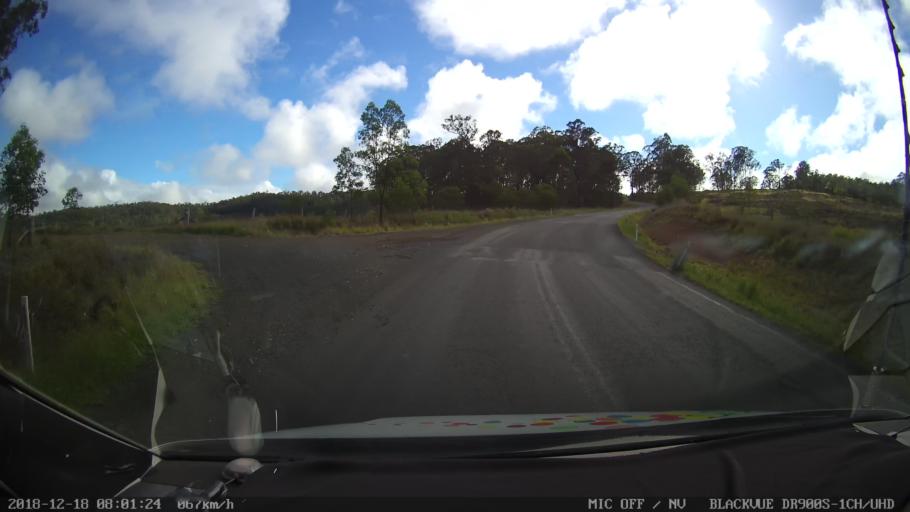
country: AU
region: New South Wales
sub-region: Kyogle
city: Kyogle
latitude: -28.3900
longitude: 152.6227
